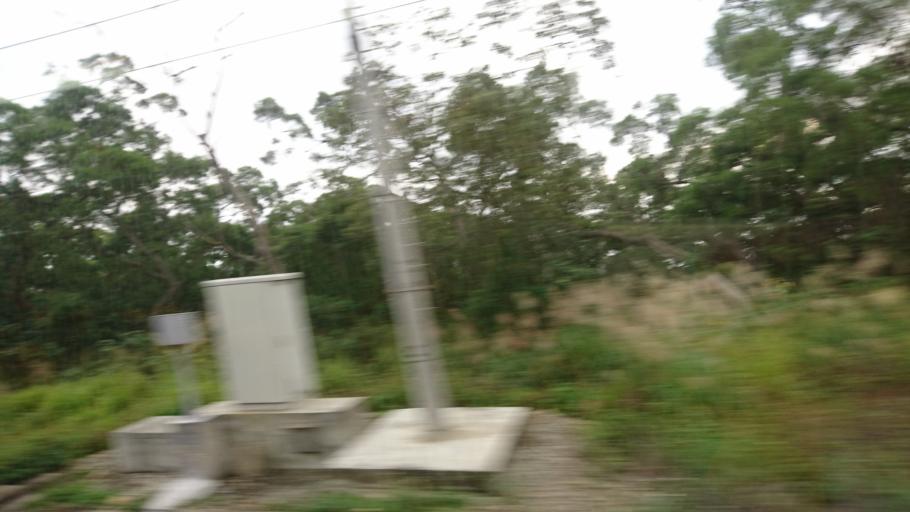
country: TW
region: Taiwan
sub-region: Hsinchu
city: Zhubei
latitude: 24.8594
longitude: 120.9983
